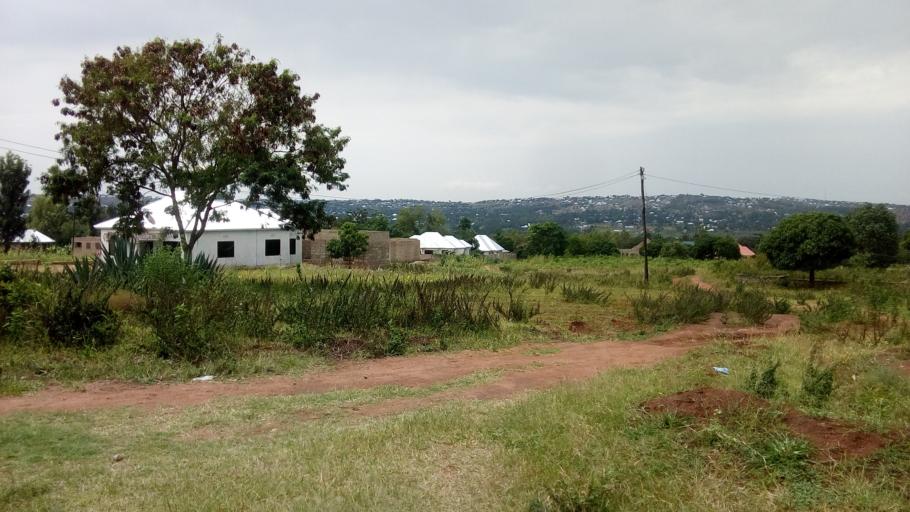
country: TZ
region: Mwanza
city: Mwanza
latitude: -2.4941
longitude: 32.9703
